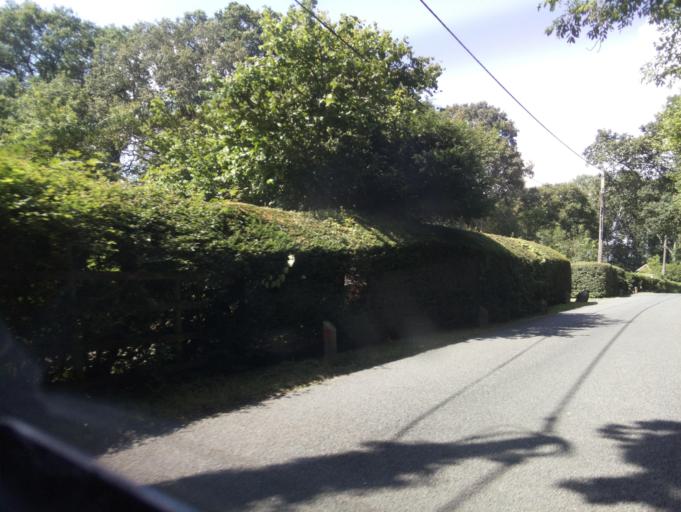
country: GB
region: England
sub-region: West Berkshire
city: Greenham
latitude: 51.3499
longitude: -1.2830
